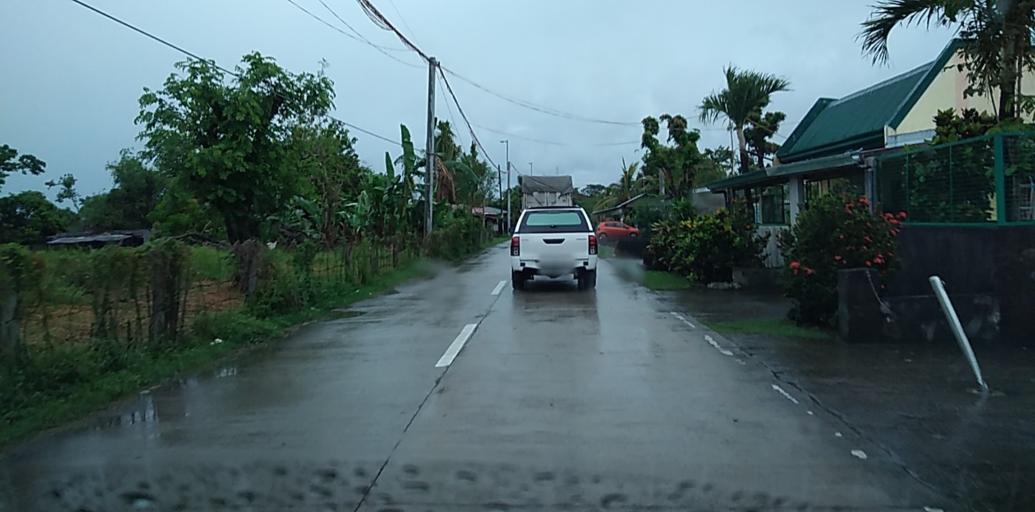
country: PH
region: Central Luzon
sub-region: Province of Pampanga
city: Salapungan
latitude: 15.1366
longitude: 120.9358
